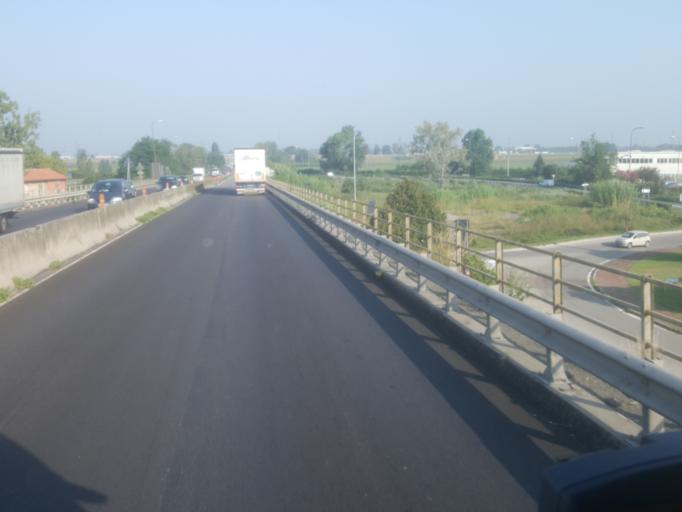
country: IT
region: Emilia-Romagna
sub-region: Provincia di Ravenna
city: Fornace Zarattini
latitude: 44.4222
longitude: 12.1627
